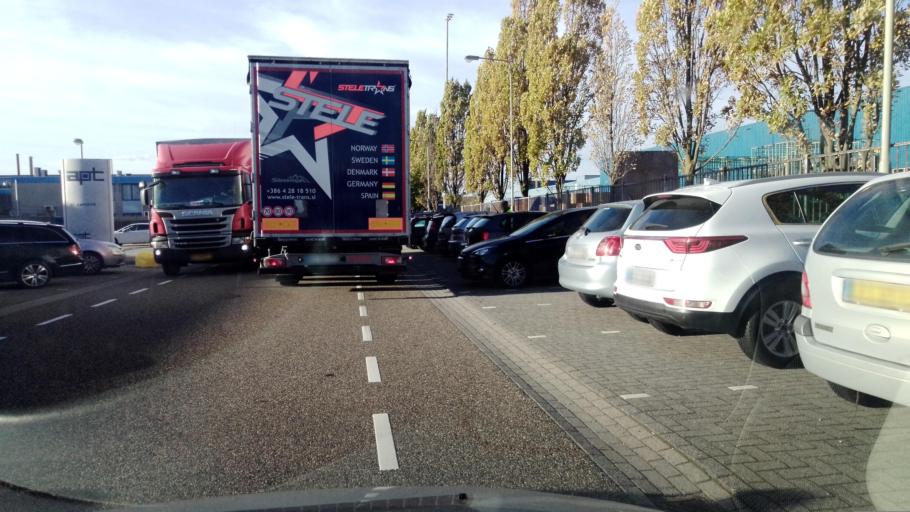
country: NL
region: Limburg
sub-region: Gemeente Roerdalen
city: Melick
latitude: 51.1708
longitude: 6.0408
